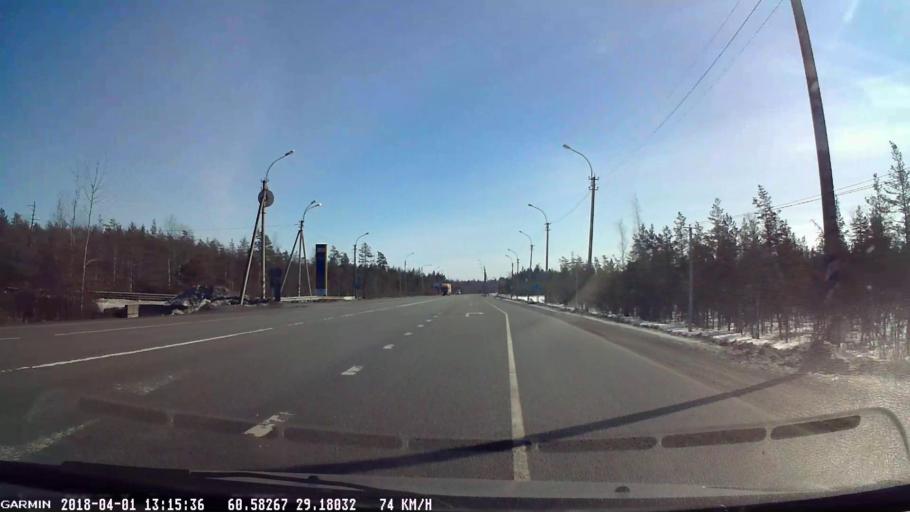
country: RU
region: Leningrad
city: Veshchevo
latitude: 60.5826
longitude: 29.1806
